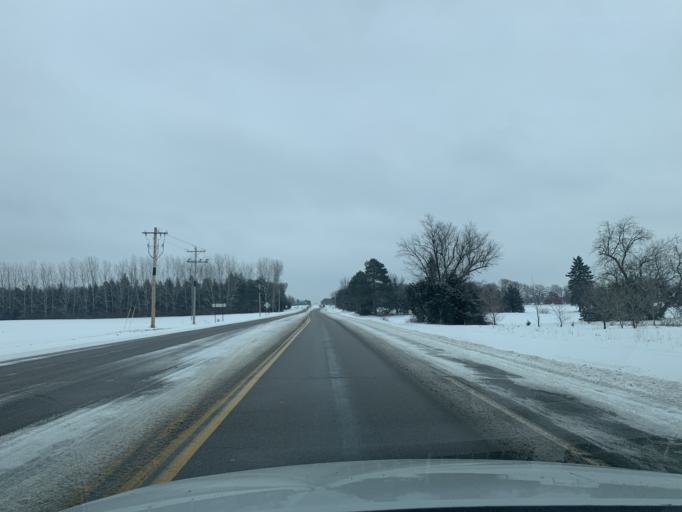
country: US
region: Minnesota
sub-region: Sherburne County
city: Zimmerman
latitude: 45.5016
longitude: -93.5920
